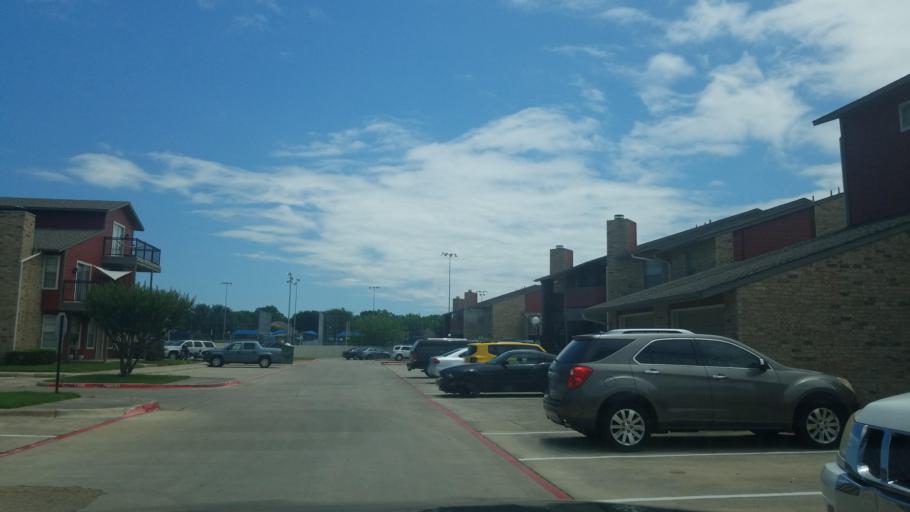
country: US
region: Texas
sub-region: Denton County
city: Denton
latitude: 33.2168
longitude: -97.1103
